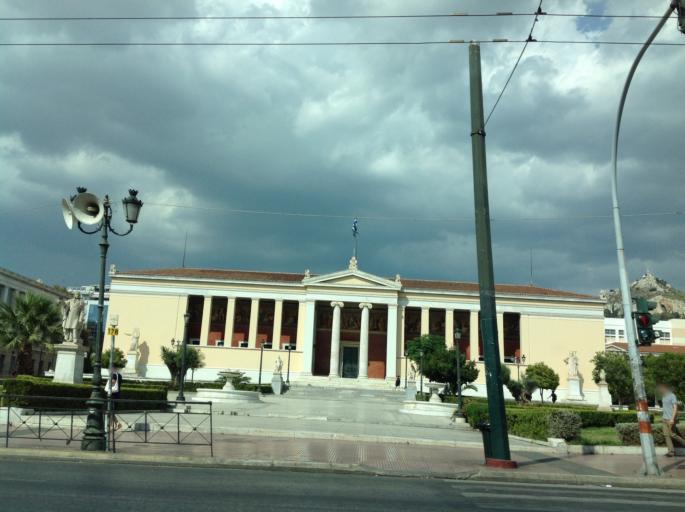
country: GR
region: Attica
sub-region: Nomarchia Athinas
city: Athens
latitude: 37.9803
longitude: 23.7330
